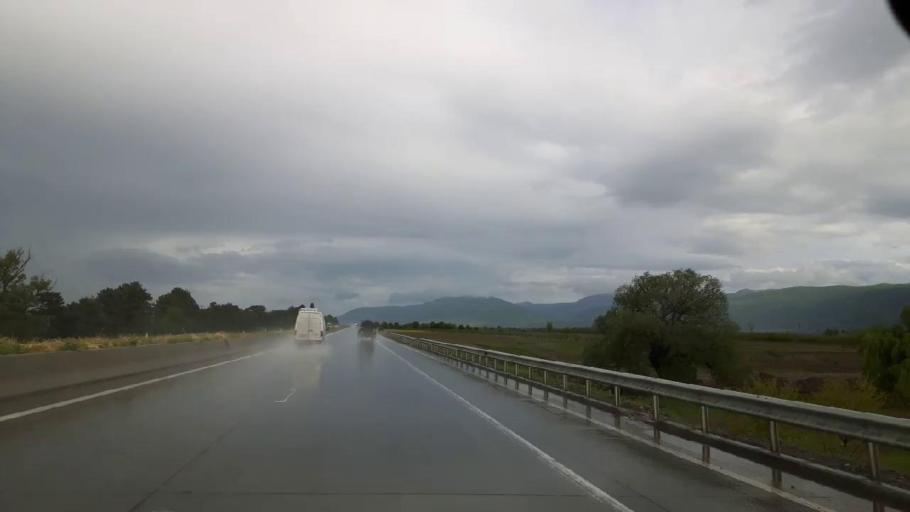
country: GE
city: Agara
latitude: 42.0423
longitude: 43.9264
